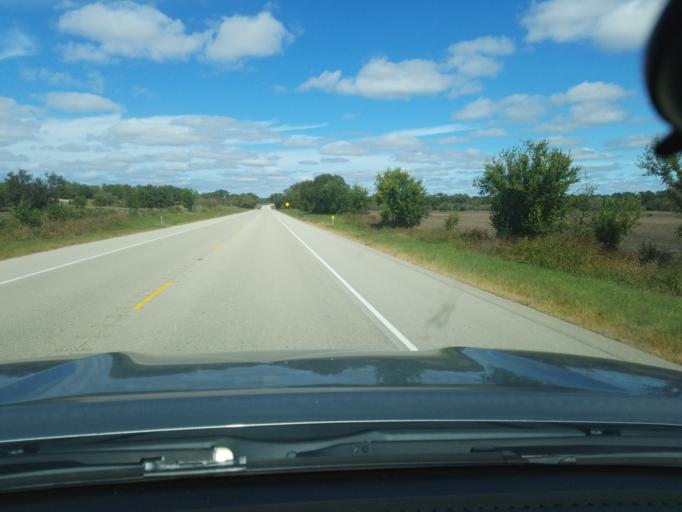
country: US
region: Texas
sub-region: Hamilton County
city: Hamilton
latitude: 31.6044
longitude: -98.1581
